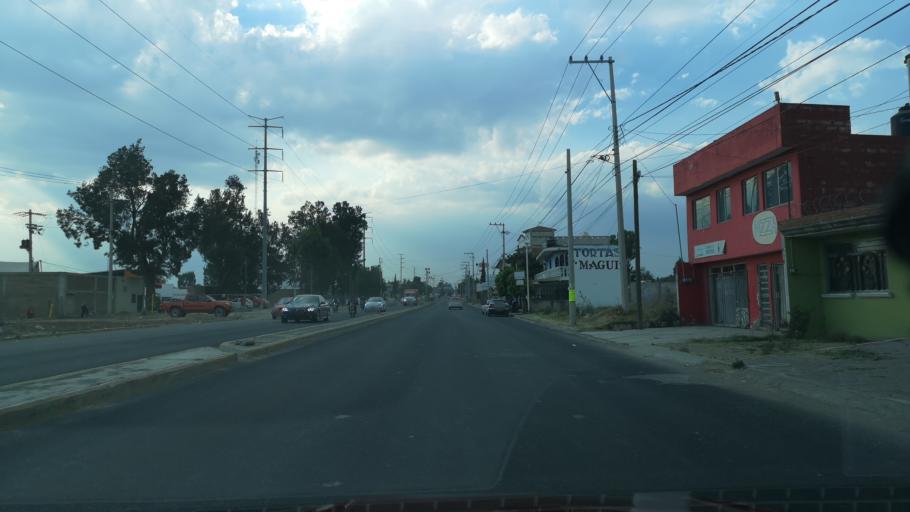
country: MX
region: Puebla
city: Cuanala
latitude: 19.0927
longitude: -98.3381
